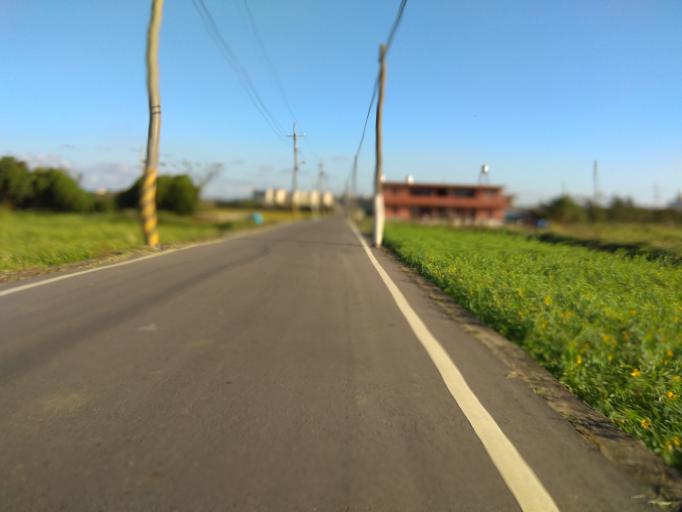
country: TW
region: Taiwan
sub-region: Hsinchu
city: Zhubei
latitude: 24.9878
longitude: 121.0506
